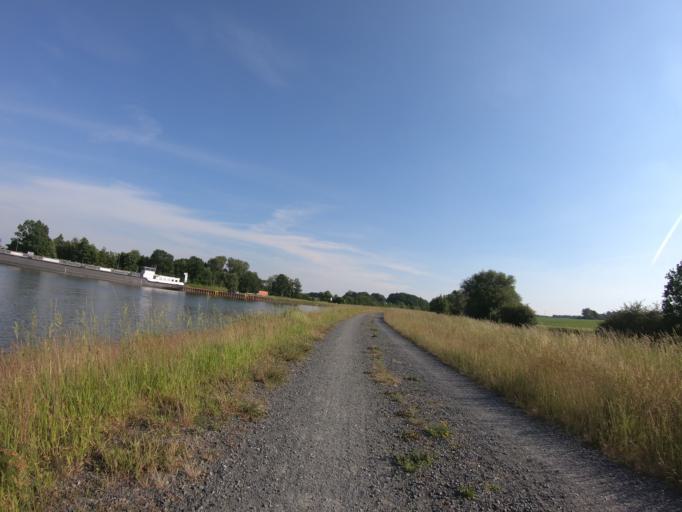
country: DE
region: Lower Saxony
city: Calberlah
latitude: 52.4071
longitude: 10.6185
